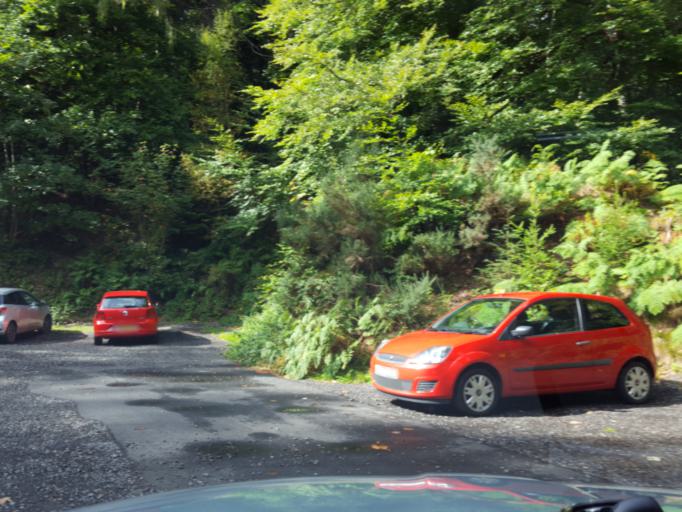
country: GB
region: Scotland
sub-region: Aberdeenshire
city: Banchory
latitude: 56.9717
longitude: -2.5789
